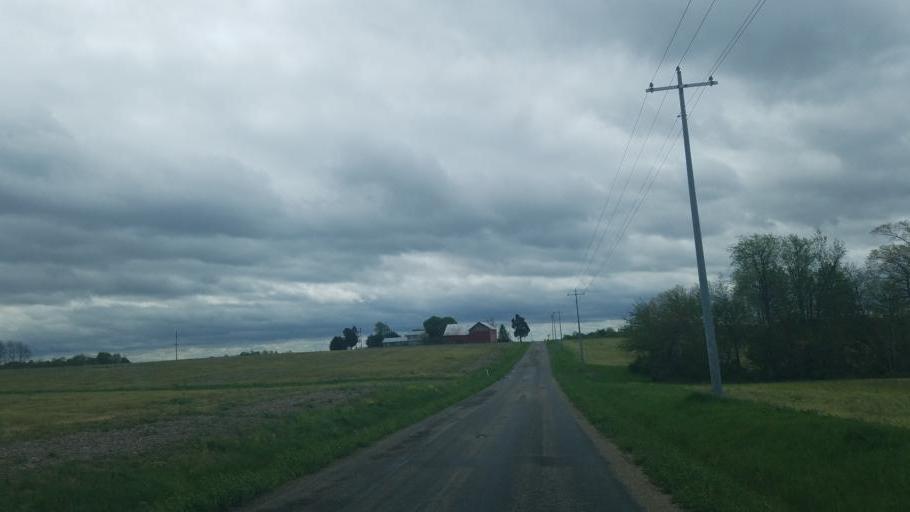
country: US
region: Ohio
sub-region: Sandusky County
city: Bellville
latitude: 40.5423
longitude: -82.4497
